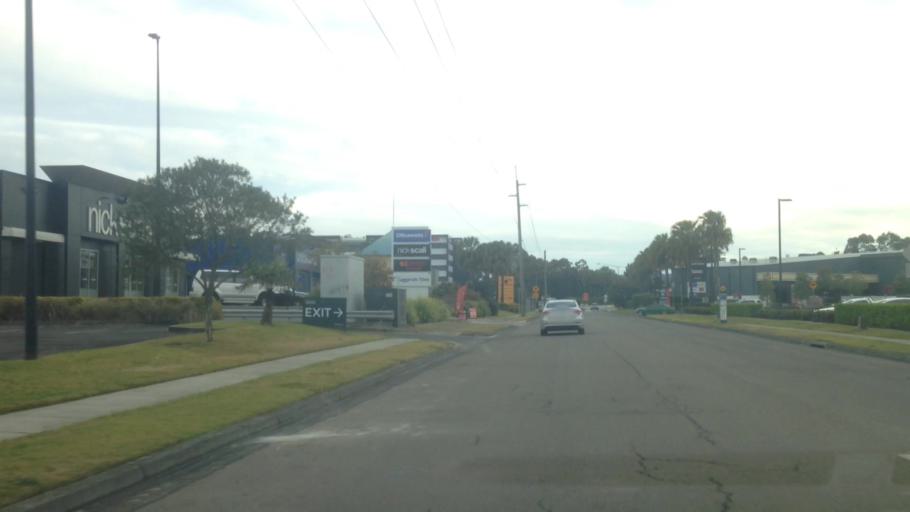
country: AU
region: New South Wales
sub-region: Wyong Shire
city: Chittaway Bay
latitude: -33.3101
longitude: 151.4227
